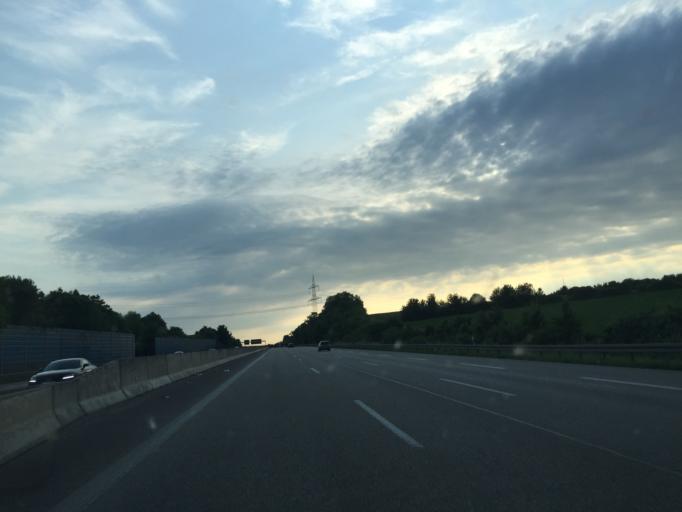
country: DE
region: Baden-Wuerttemberg
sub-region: Karlsruhe Region
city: Rauenberg
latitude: 49.2758
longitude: 8.6937
